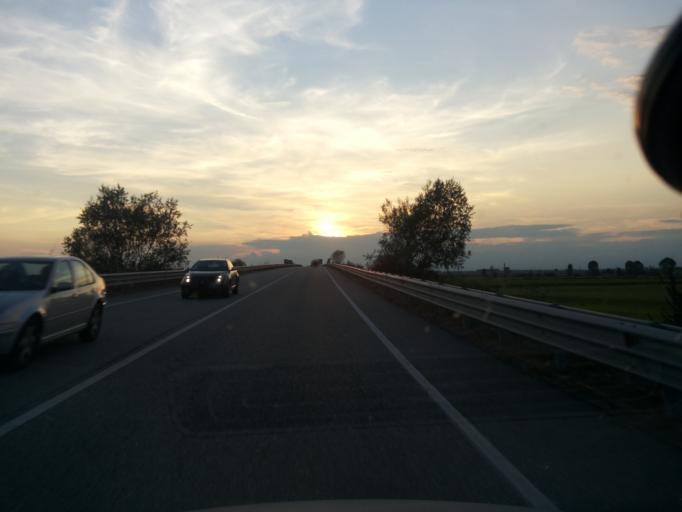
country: IT
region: Piedmont
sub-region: Provincia di Vercelli
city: Borgo Vercelli
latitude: 45.3641
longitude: 8.4716
